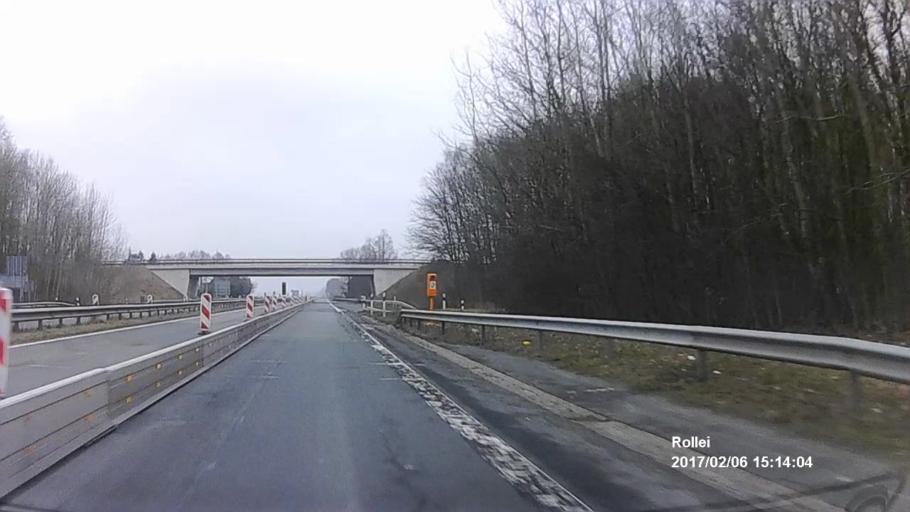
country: DE
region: Lower Saxony
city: Leer
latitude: 53.3122
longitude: 7.4619
